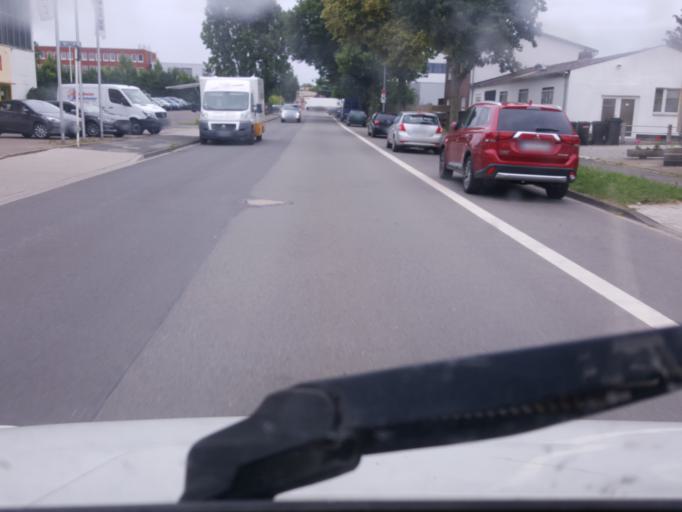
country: DE
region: North Rhine-Westphalia
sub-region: Regierungsbezirk Detmold
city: Minden
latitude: 52.2997
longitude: 8.9002
